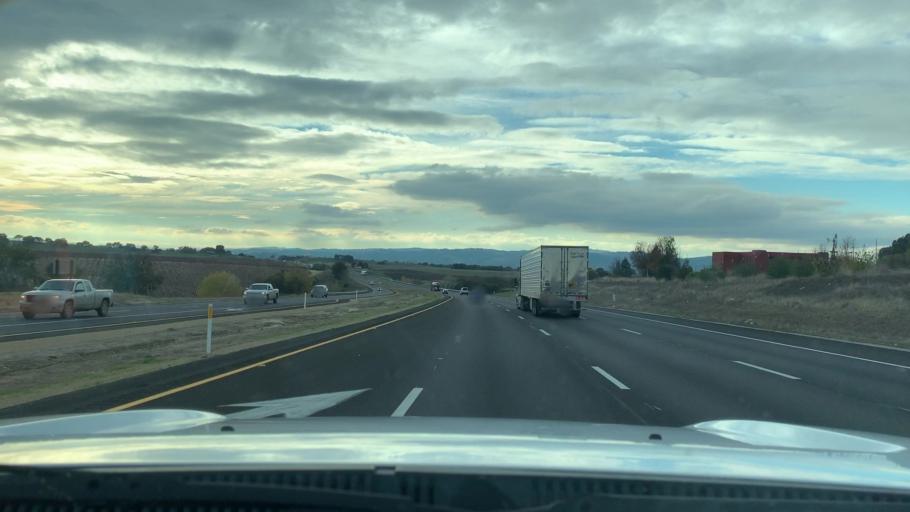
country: US
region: California
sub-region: San Luis Obispo County
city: Paso Robles
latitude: 35.6592
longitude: -120.6052
